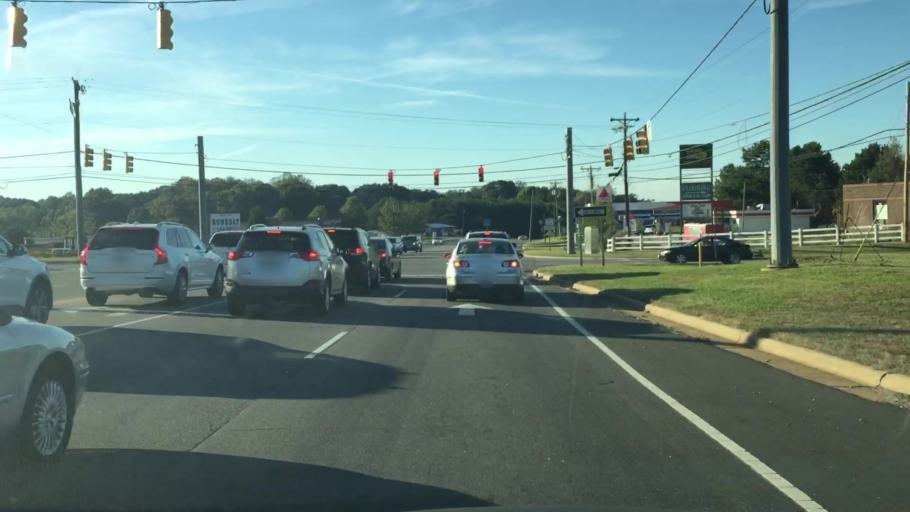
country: US
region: North Carolina
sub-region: Gaston County
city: Davidson
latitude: 35.5544
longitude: -80.8594
